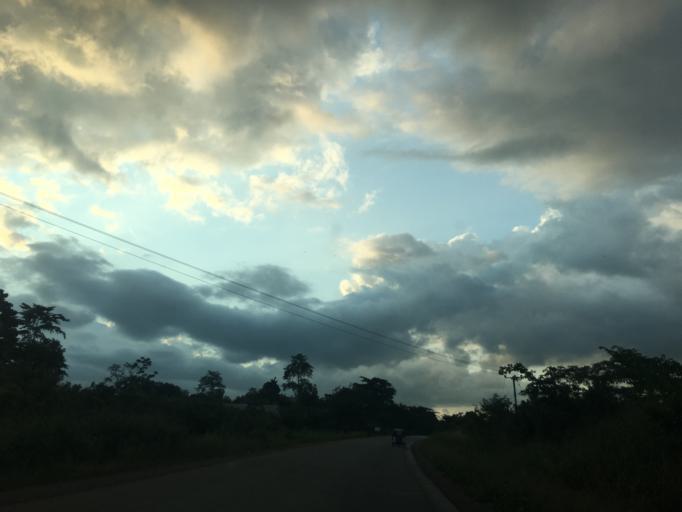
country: GH
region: Western
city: Bibiani
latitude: 6.7674
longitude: -2.5096
